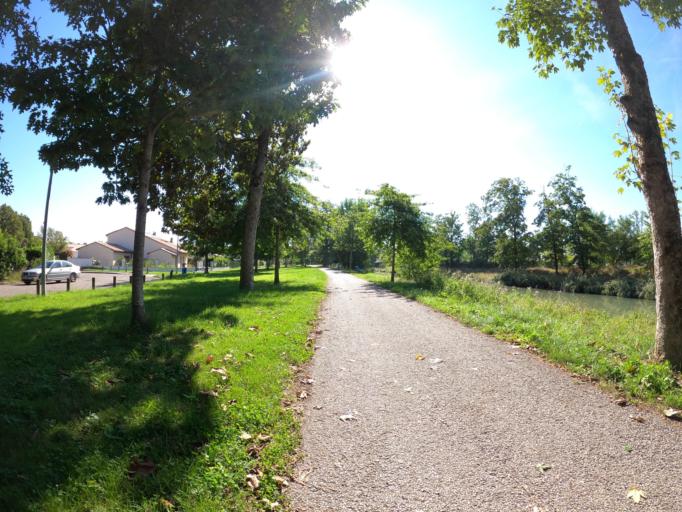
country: FR
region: Aquitaine
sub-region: Departement du Lot-et-Garonne
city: Bon-Encontre
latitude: 44.1866
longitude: 0.6530
